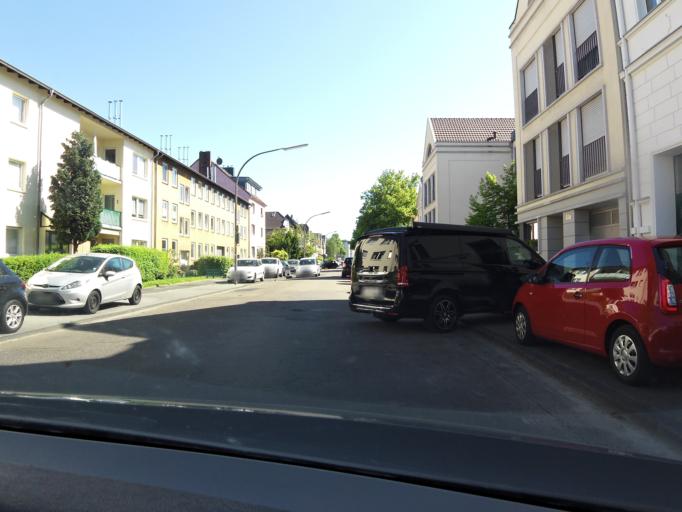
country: DE
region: North Rhine-Westphalia
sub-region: Regierungsbezirk Koln
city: Mengenich
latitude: 50.9397
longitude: 6.8893
